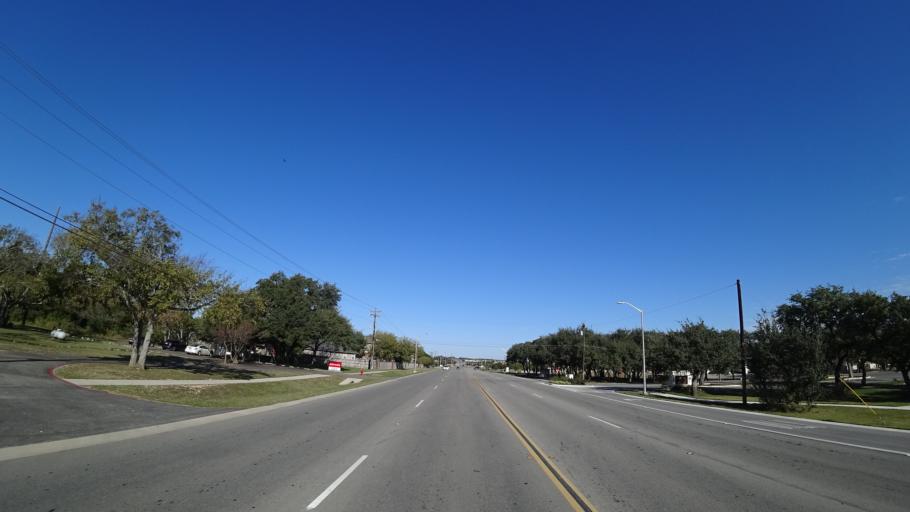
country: US
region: Texas
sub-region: Williamson County
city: Cedar Park
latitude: 30.5259
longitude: -97.8434
